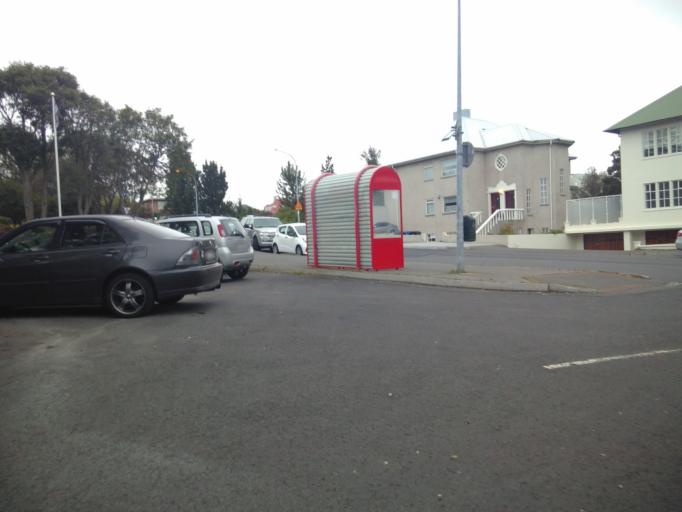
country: IS
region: Capital Region
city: Reykjavik
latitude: 64.1390
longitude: -21.9094
